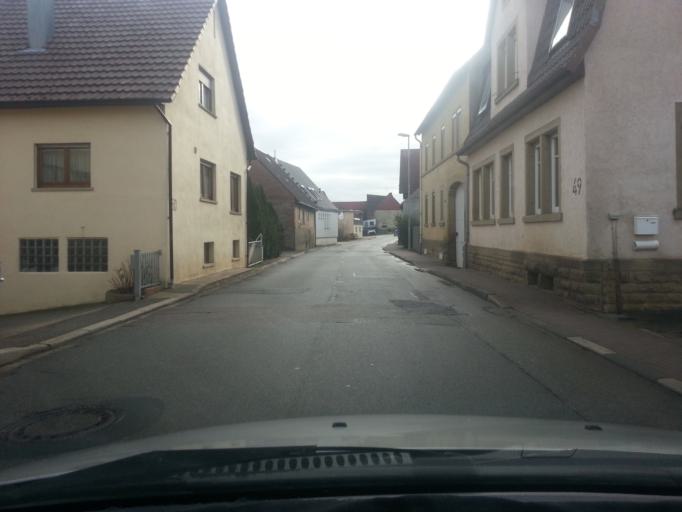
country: DE
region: Baden-Wuerttemberg
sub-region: Regierungsbezirk Stuttgart
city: Eppingen
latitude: 49.1688
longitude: 8.8891
